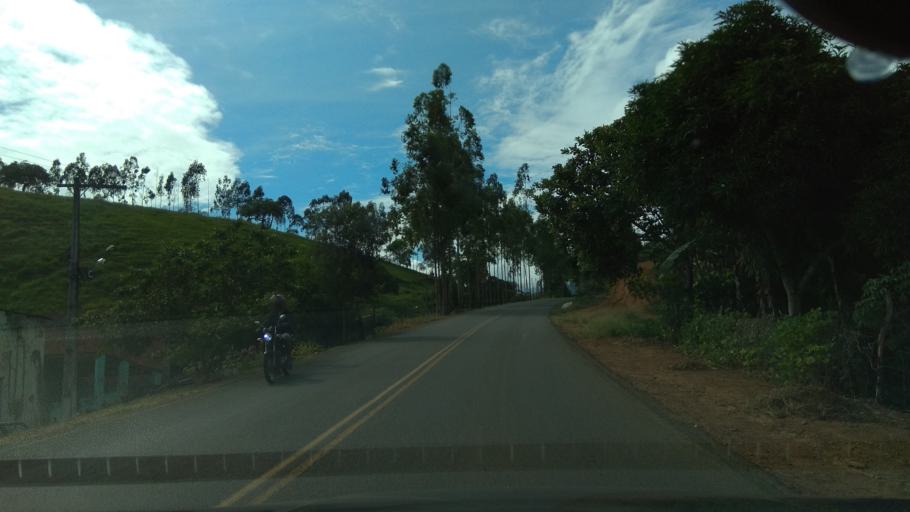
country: BR
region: Bahia
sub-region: Ubaira
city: Ubaira
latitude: -13.2708
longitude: -39.6401
